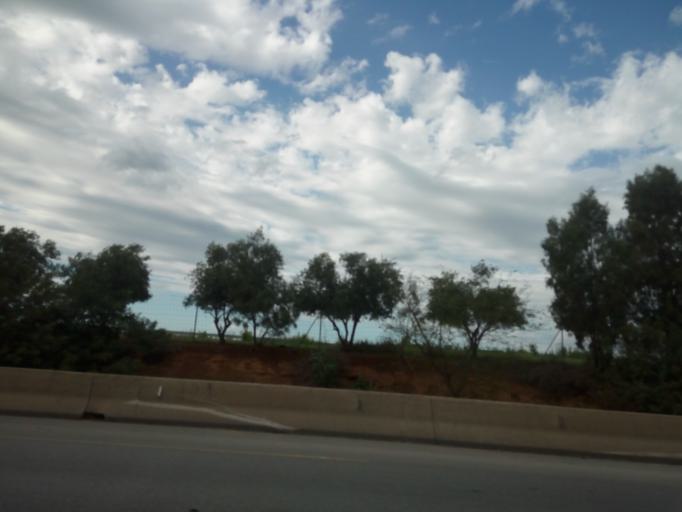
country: DZ
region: Tipaza
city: Mouzaia
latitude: 36.4497
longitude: 2.6643
